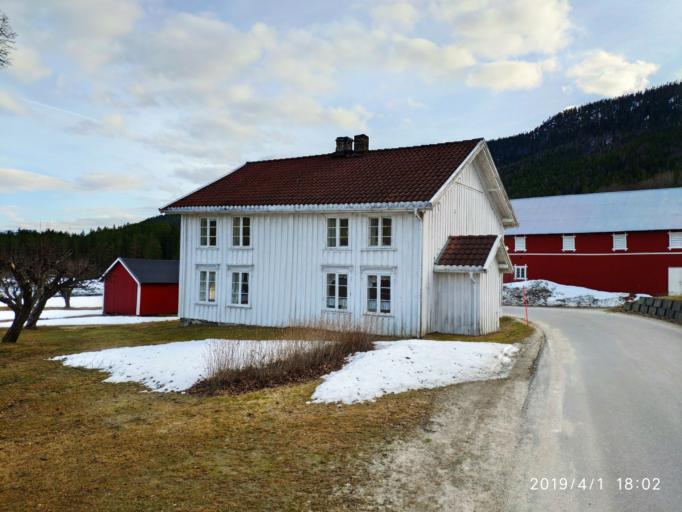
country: NO
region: Telemark
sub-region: Nissedal
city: Treungen
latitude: 59.1181
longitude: 8.4715
